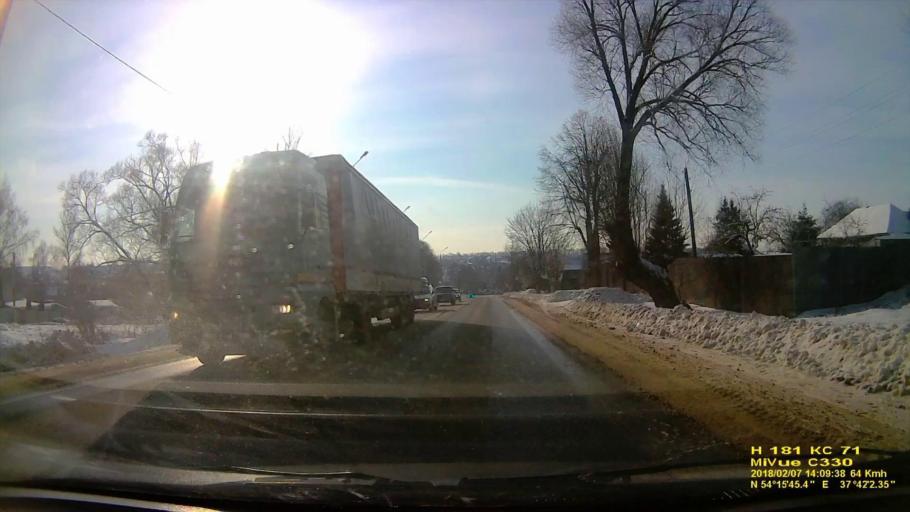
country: RU
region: Tula
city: Gorelki
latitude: 54.2626
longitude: 37.7006
